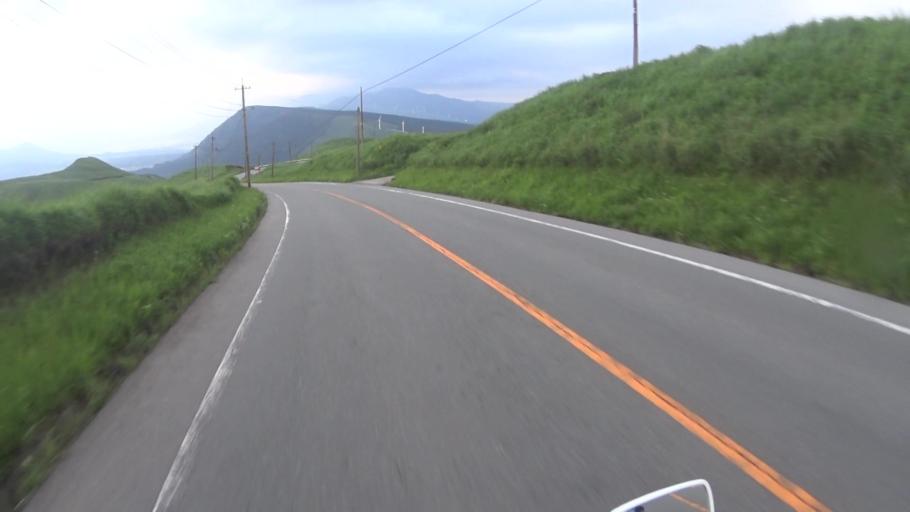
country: JP
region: Kumamoto
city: Aso
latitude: 32.9272
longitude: 130.9678
